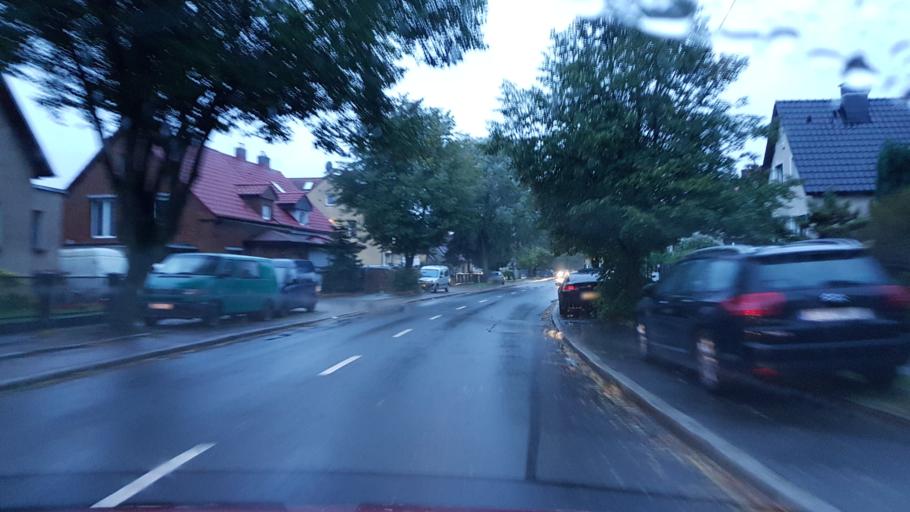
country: PL
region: West Pomeranian Voivodeship
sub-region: Powiat policki
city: Przeclaw
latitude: 53.4125
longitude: 14.5024
